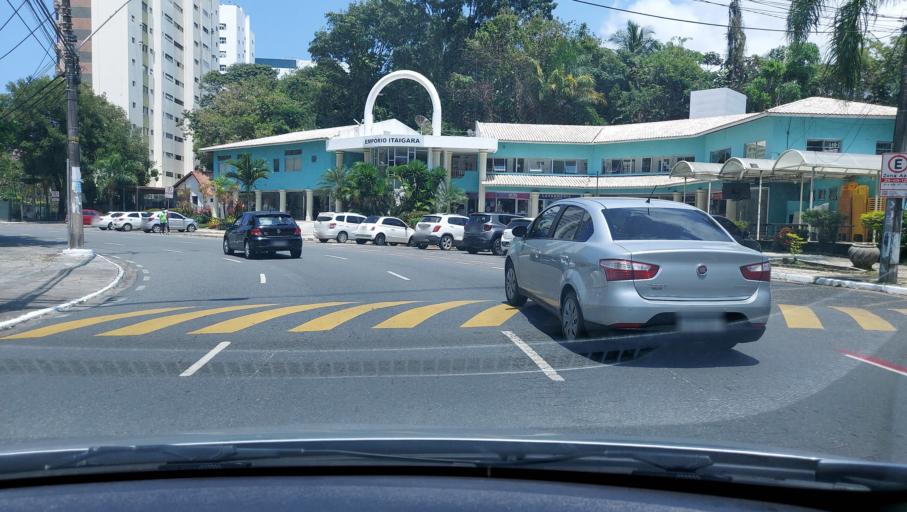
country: BR
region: Bahia
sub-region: Salvador
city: Salvador
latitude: -12.9923
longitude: -38.4623
